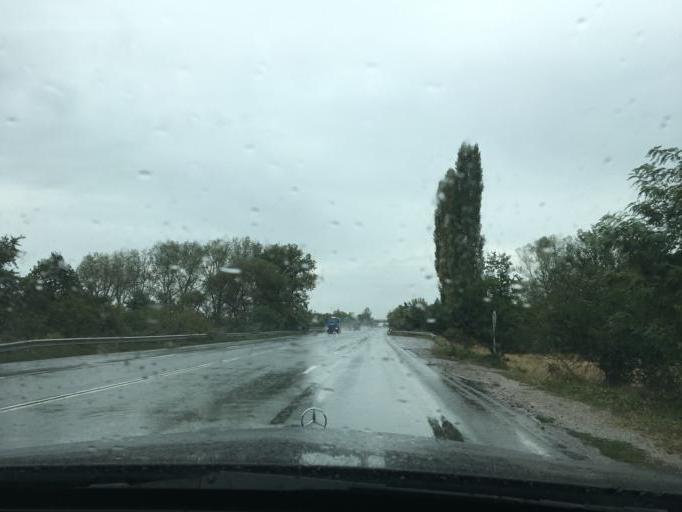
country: BG
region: Sofiya
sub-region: Obshtina Bozhurishte
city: Bozhurishte
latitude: 42.7949
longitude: 23.1466
